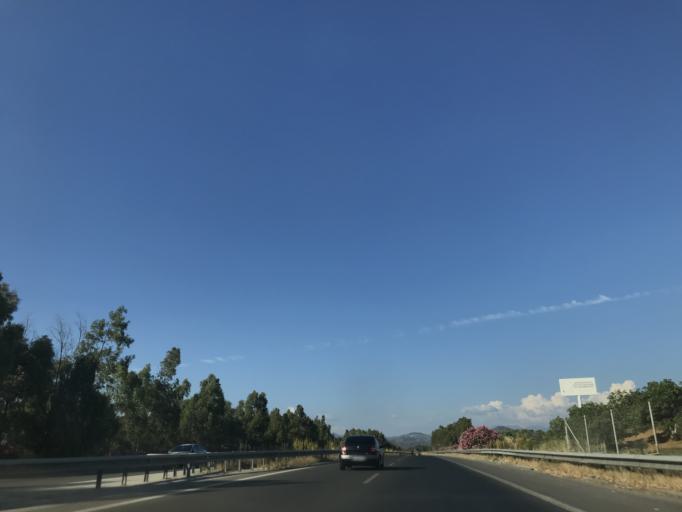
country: TR
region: Aydin
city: Germencik
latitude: 37.8515
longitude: 27.5498
